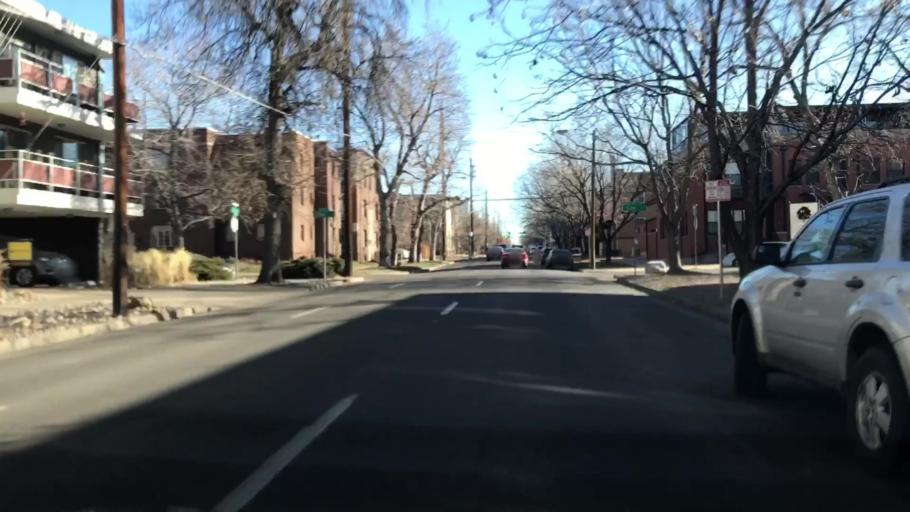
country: US
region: Colorado
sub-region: Denver County
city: Denver
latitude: 39.7384
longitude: -104.9627
